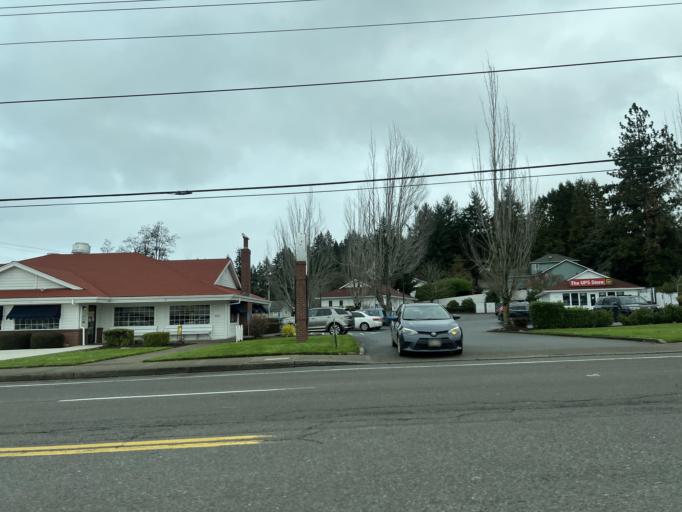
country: US
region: Oregon
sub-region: Marion County
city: Salem
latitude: 44.8869
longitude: -123.0331
